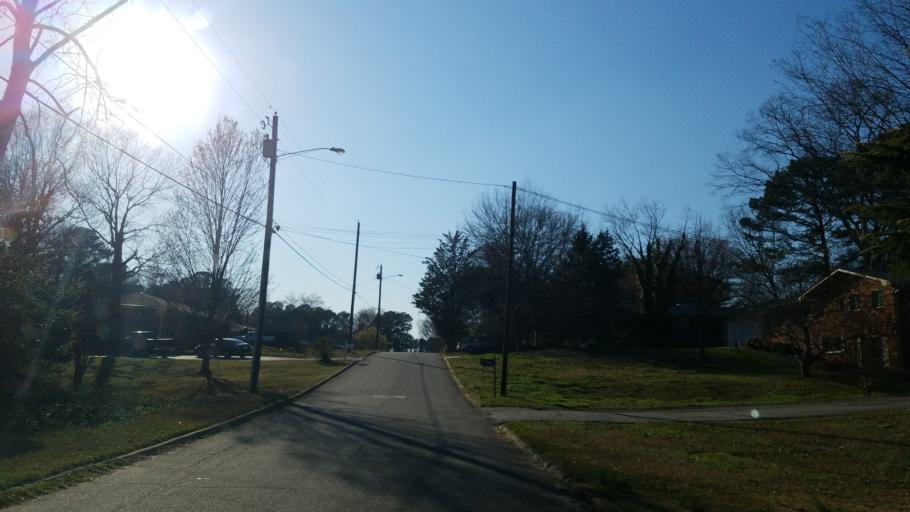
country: US
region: Georgia
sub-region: Cobb County
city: Marietta
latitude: 33.9962
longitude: -84.4994
